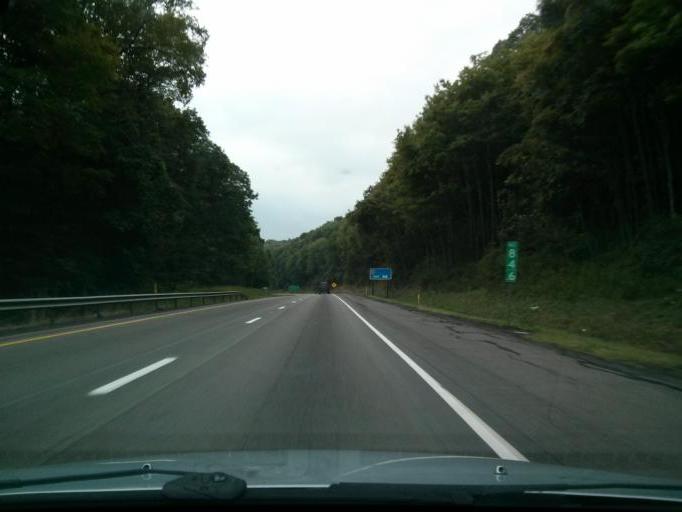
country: US
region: Pennsylvania
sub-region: Jefferson County
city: Brookville
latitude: 41.1522
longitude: -78.9991
